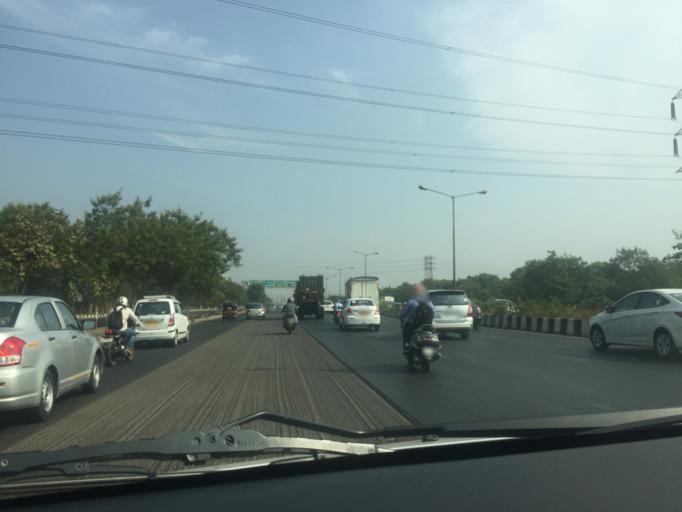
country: IN
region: Maharashtra
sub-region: Thane
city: Airoli
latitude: 19.1456
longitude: 72.9510
